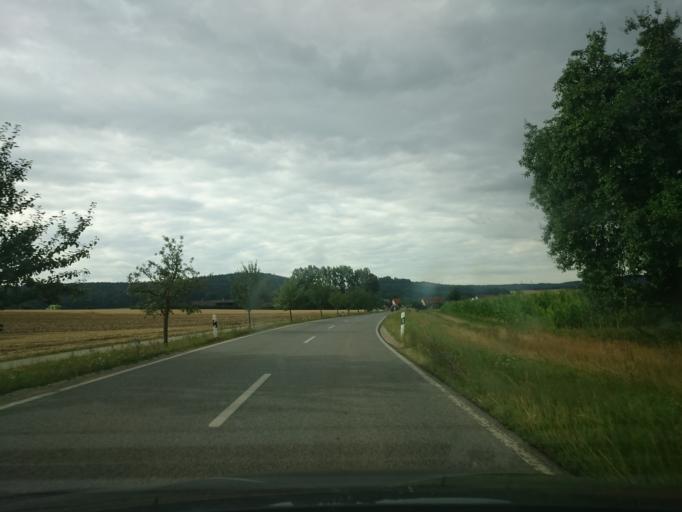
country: DE
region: Bavaria
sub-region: Regierungsbezirk Mittelfranken
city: Thalmassing
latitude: 49.1383
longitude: 11.2135
